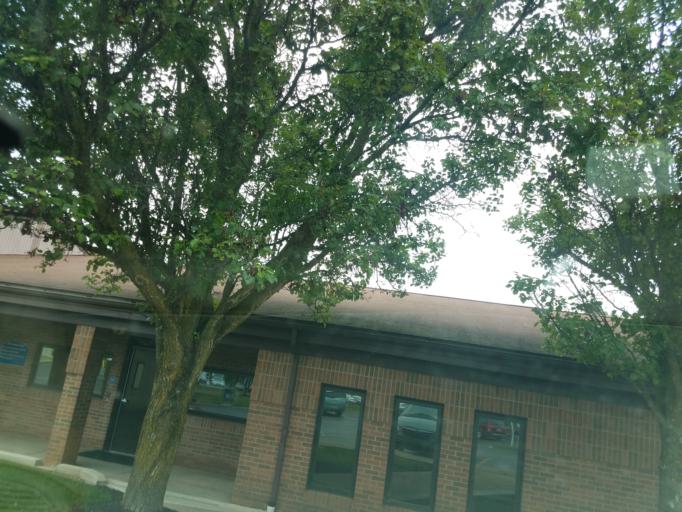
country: US
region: Ohio
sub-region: Knox County
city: Mount Vernon
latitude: 40.4002
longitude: -82.4495
